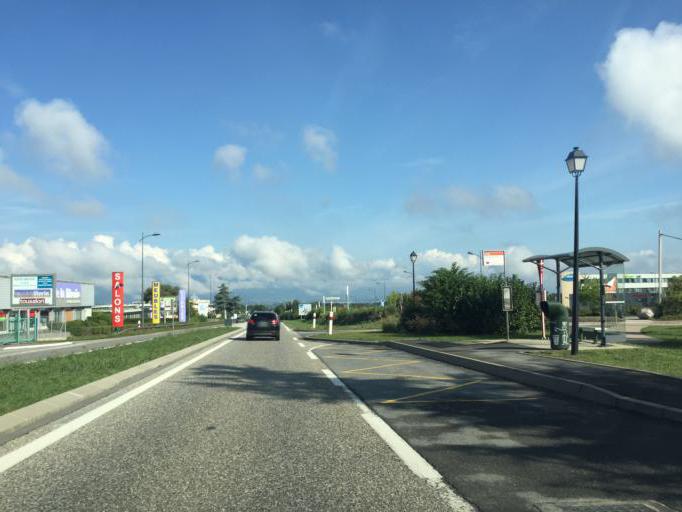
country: FR
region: Rhone-Alpes
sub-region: Departement de la Haute-Savoie
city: Neydens
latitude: 46.1202
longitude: 6.0951
